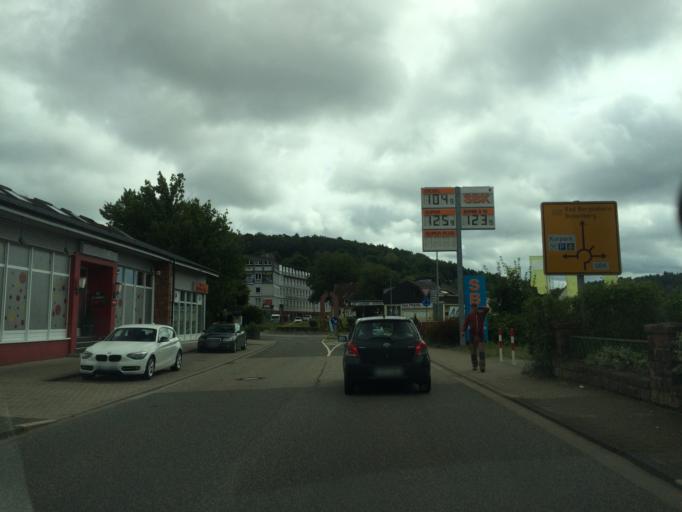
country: DE
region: Rheinland-Pfalz
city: Dahn
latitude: 49.1490
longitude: 7.7801
